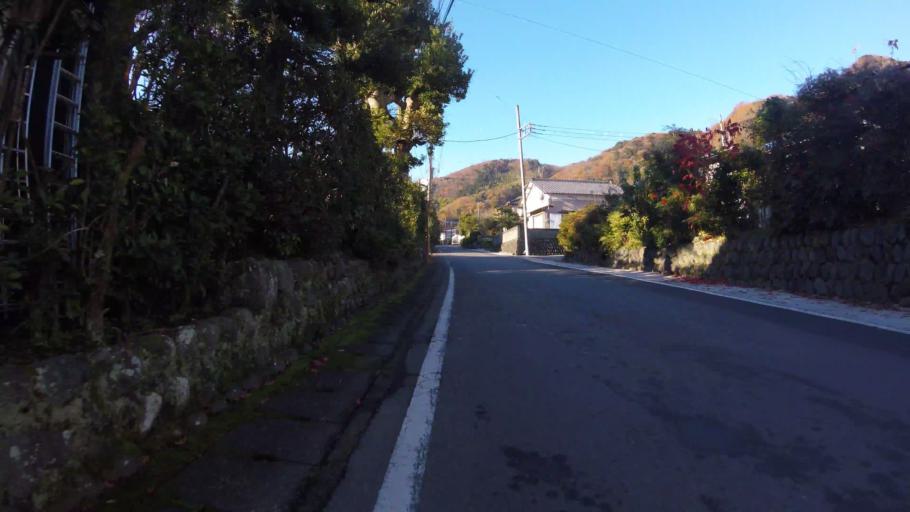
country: JP
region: Shizuoka
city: Ito
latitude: 34.9645
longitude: 138.9401
